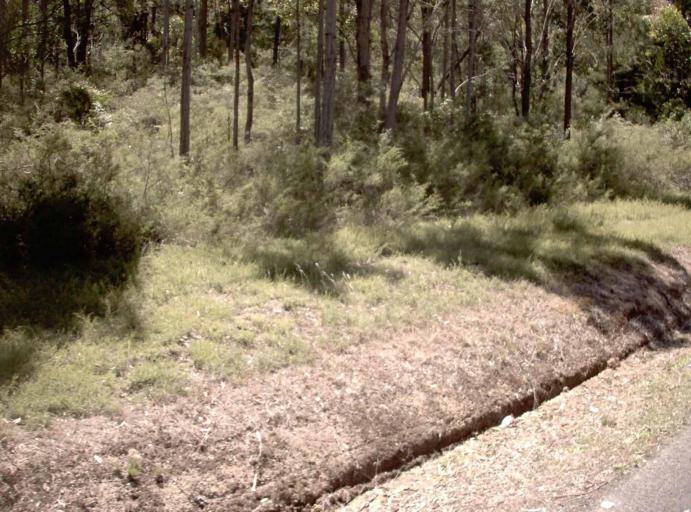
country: AU
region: Victoria
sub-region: East Gippsland
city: Lakes Entrance
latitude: -37.7559
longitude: 148.0650
